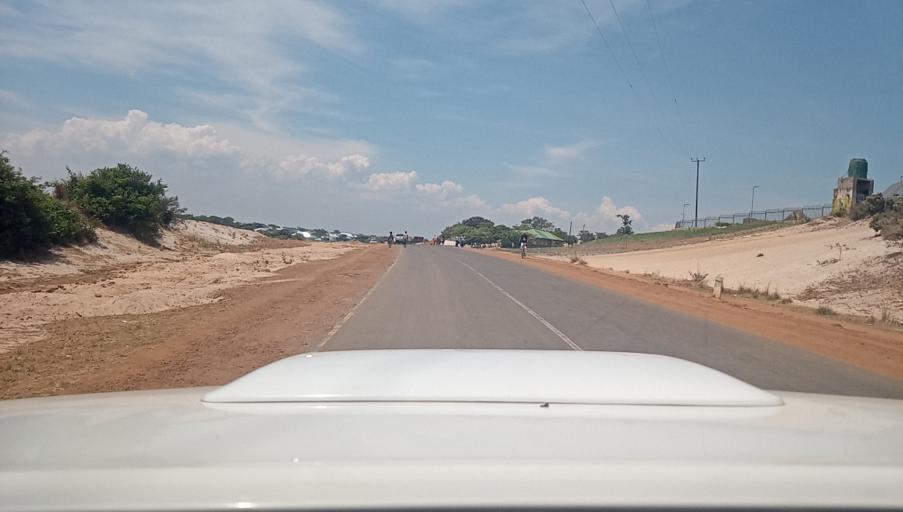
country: ZM
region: Luapula
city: Samfya
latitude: -11.3503
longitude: 29.5580
